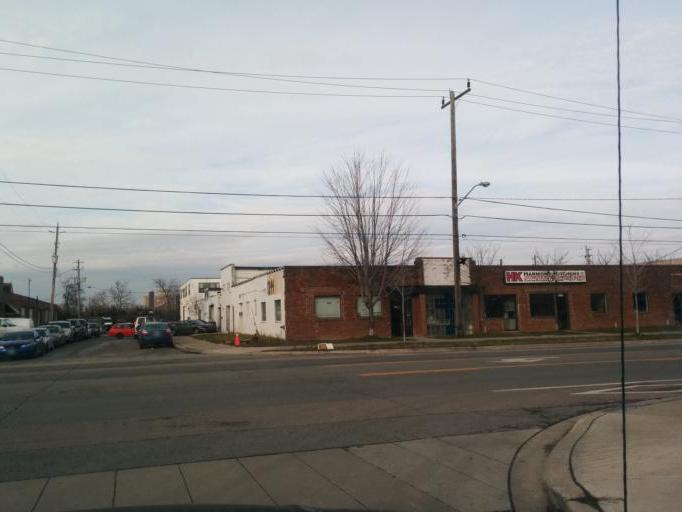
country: CA
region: Ontario
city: Etobicoke
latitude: 43.6015
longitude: -79.5138
